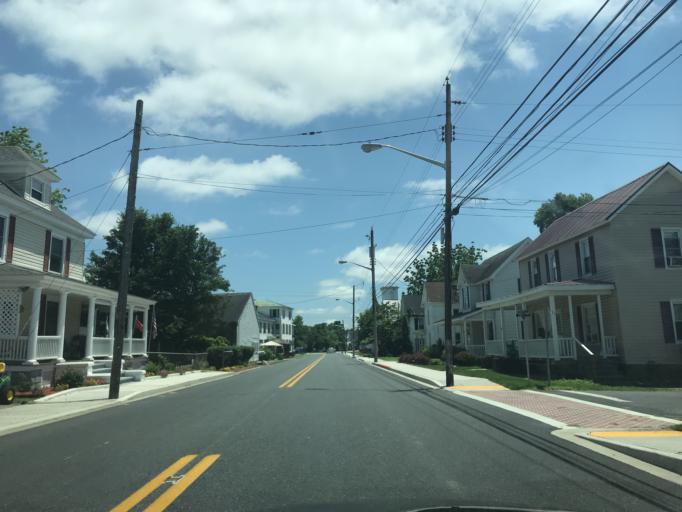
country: US
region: Maryland
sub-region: Dorchester County
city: Hurlock
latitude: 38.6363
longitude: -75.8659
